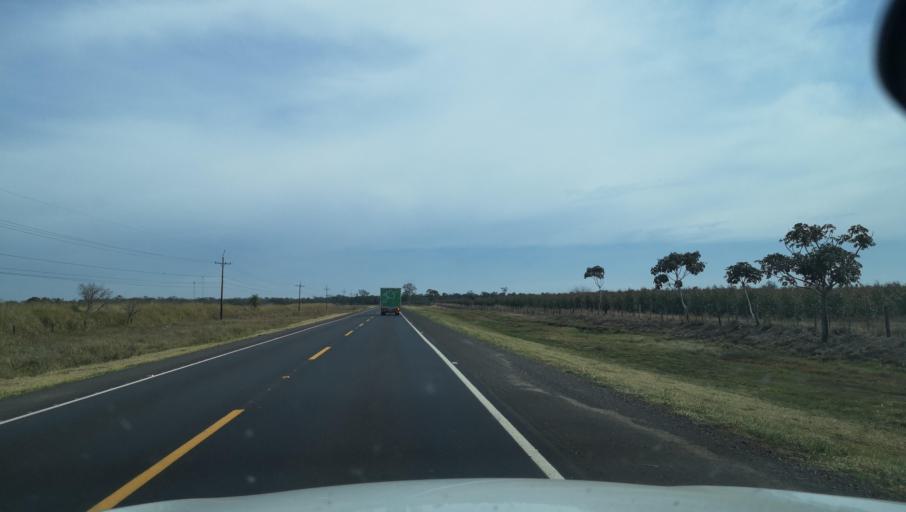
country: PY
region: Itapua
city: General Delgado
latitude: -27.1126
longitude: -56.3659
